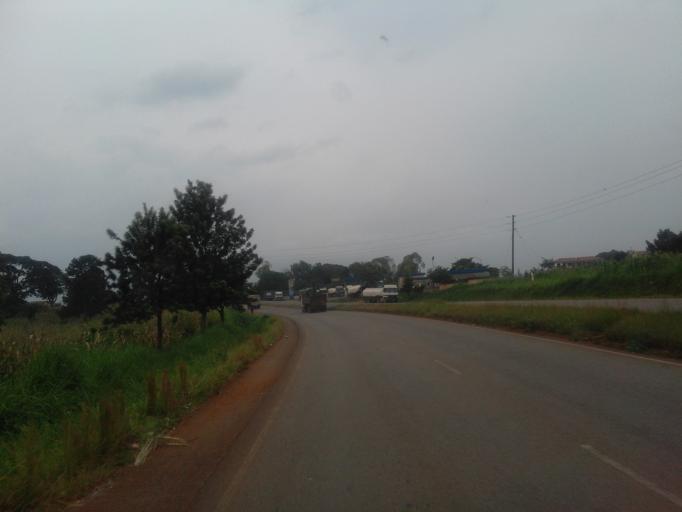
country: UG
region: Eastern Region
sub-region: Jinja District
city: Jinja
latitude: 0.4422
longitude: 33.2096
